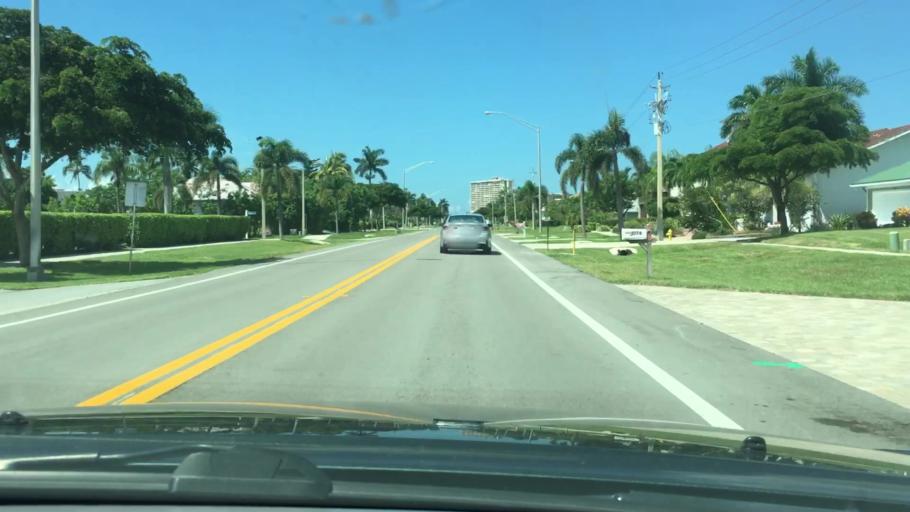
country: US
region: Florida
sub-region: Collier County
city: Marco
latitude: 25.9371
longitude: -81.7205
